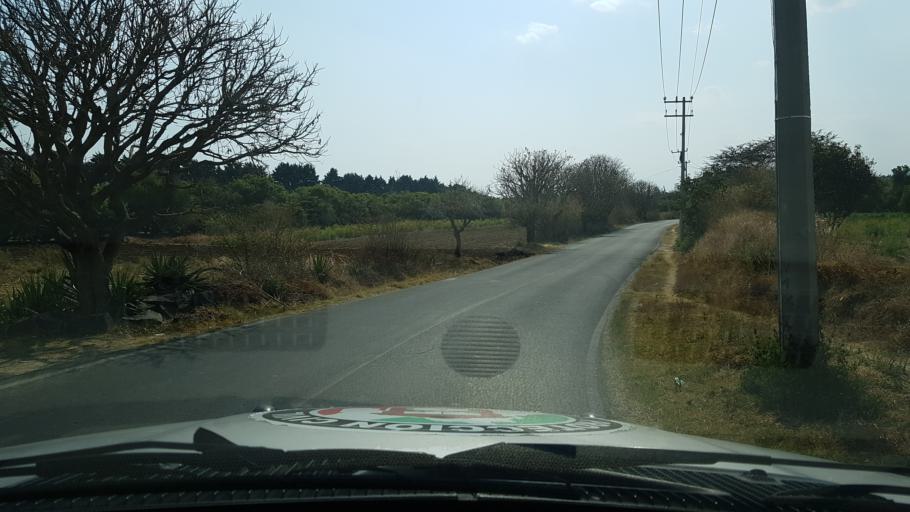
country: MX
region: Mexico
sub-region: Ozumba
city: San Jose Tlacotitlan
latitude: 18.9871
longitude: -98.8138
